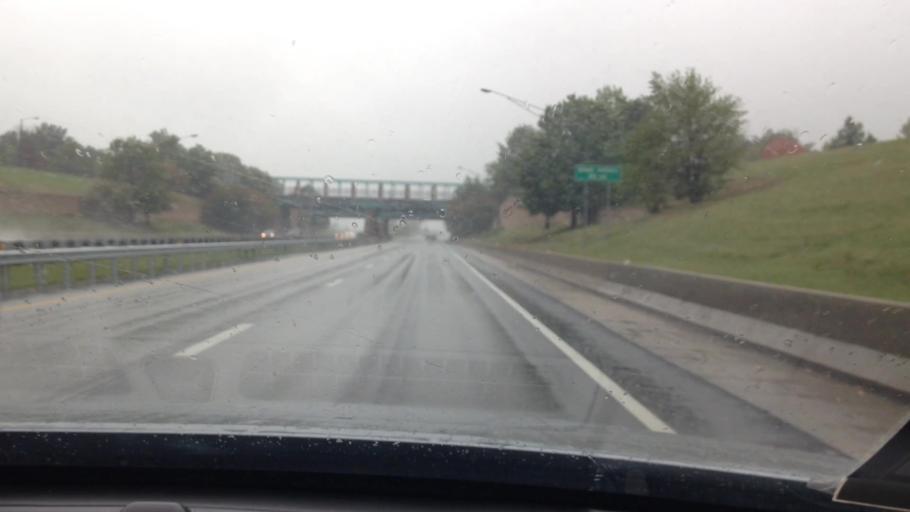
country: US
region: Kansas
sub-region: Johnson County
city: Mission Hills
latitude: 39.0095
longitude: -94.5549
